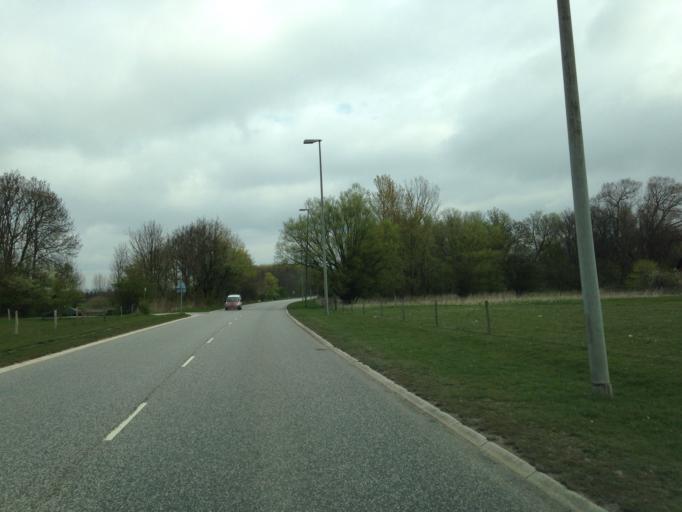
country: DK
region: Capital Region
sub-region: Ishoj Kommune
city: Ishoj
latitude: 55.6068
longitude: 12.3273
